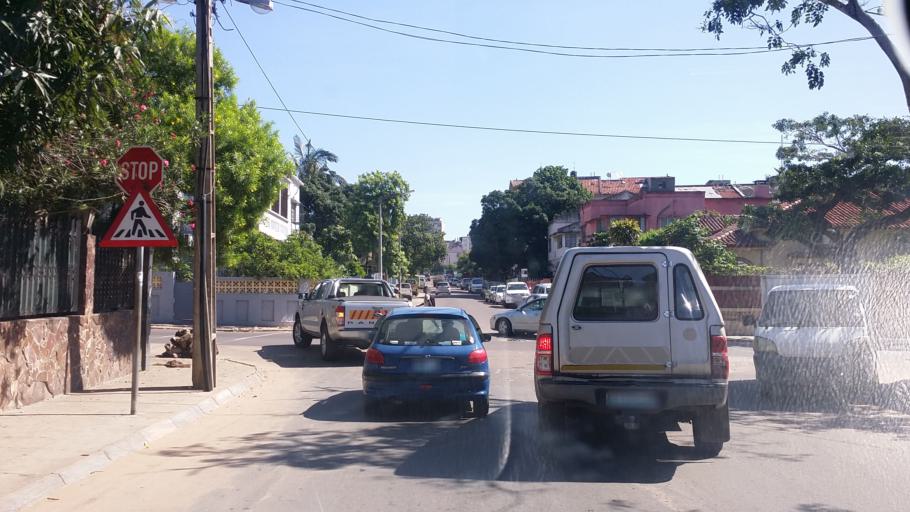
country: MZ
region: Maputo City
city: Maputo
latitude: -25.9574
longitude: 32.5786
